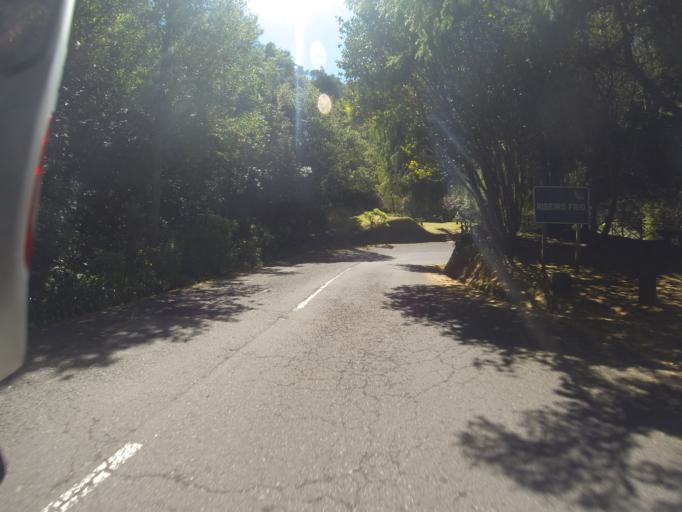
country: PT
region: Madeira
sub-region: Santana
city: Santana
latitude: 32.7335
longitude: -16.8873
